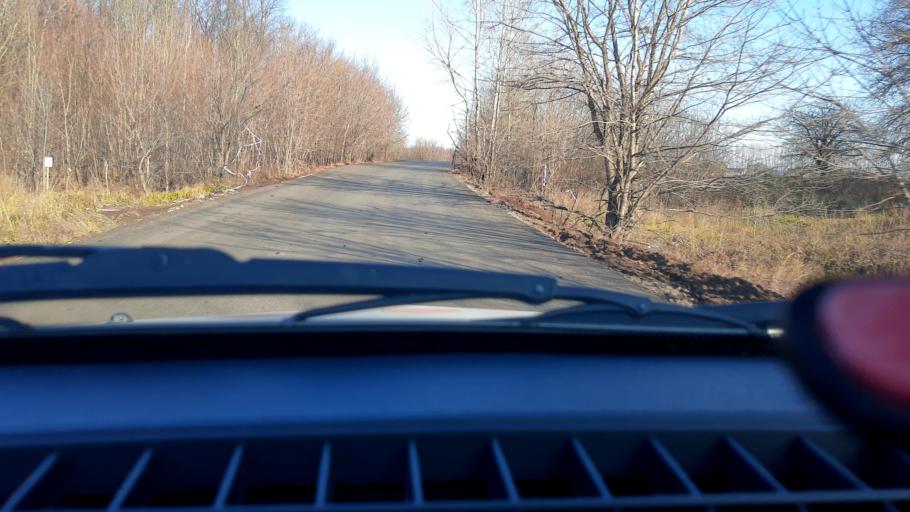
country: RU
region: Bashkortostan
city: Kabakovo
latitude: 54.6167
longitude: 56.1521
